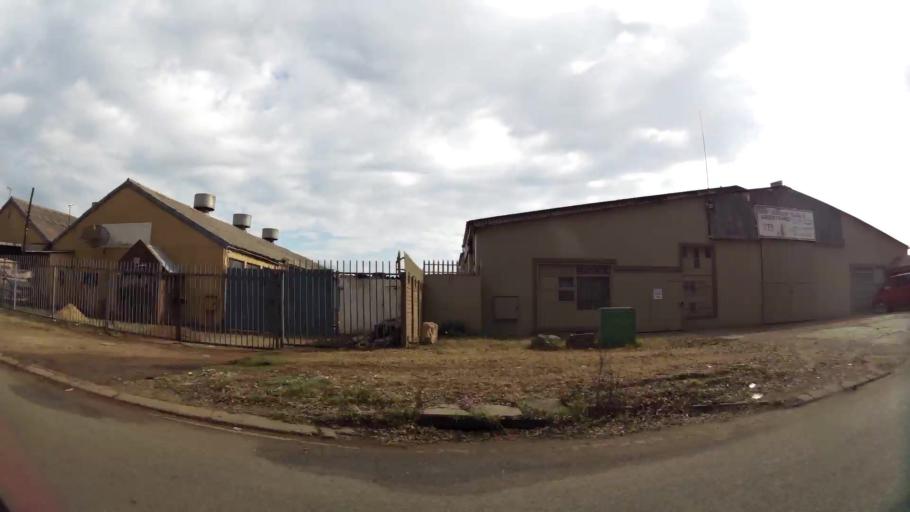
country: ZA
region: Gauteng
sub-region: Sedibeng District Municipality
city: Vanderbijlpark
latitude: -26.6894
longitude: 27.8095
